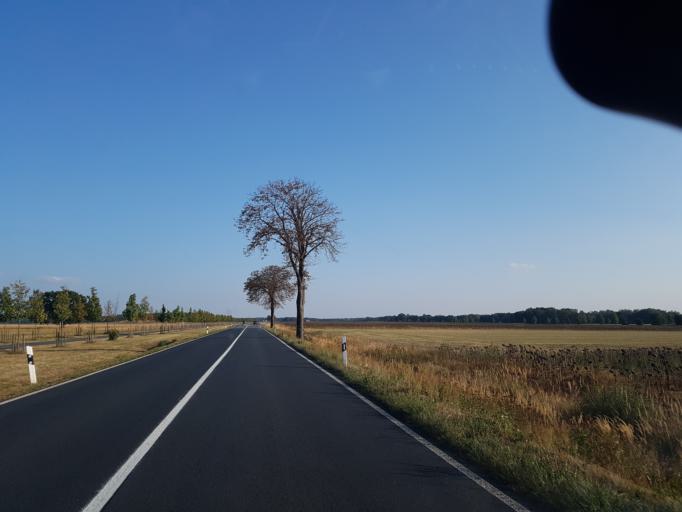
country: DE
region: Brandenburg
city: Herzberg
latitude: 51.6816
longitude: 13.2608
